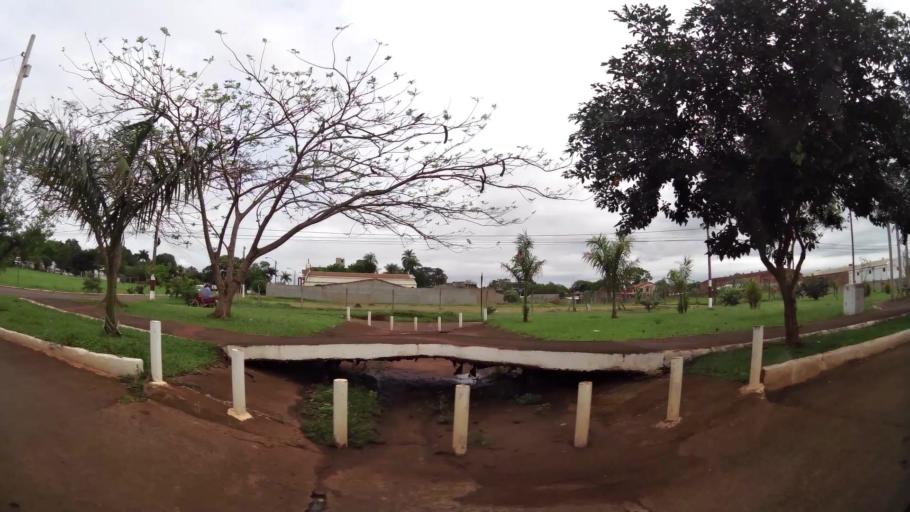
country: PY
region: Alto Parana
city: Ciudad del Este
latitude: -25.4052
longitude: -54.6363
